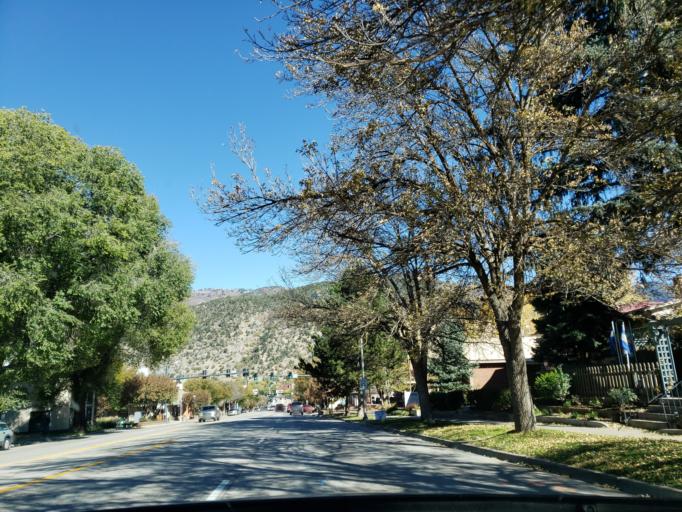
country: US
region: Colorado
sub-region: Garfield County
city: Glenwood Springs
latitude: 39.5433
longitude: -107.3248
